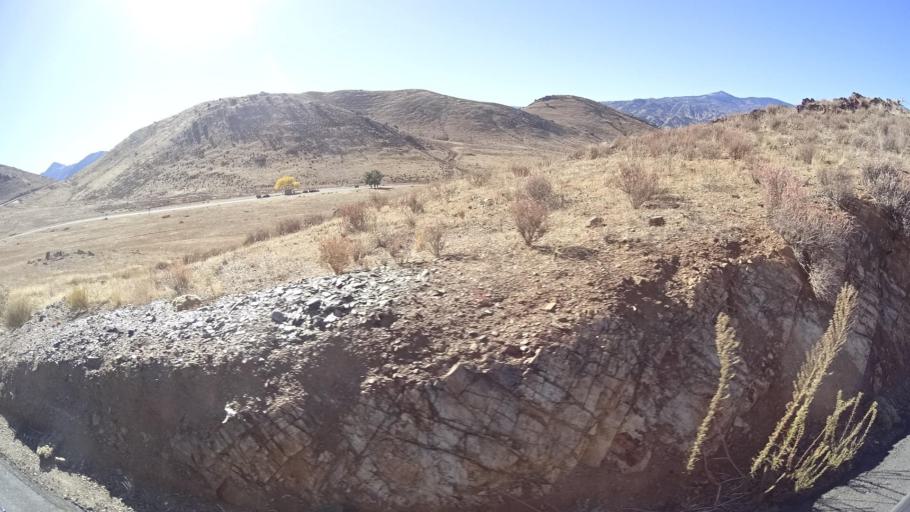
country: US
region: California
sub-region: Kern County
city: Wofford Heights
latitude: 35.6929
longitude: -118.4261
